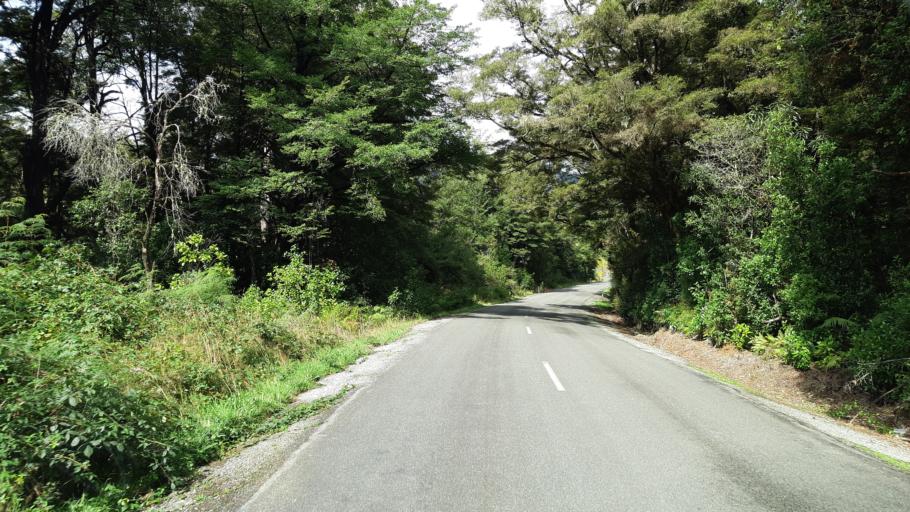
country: NZ
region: West Coast
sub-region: Buller District
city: Westport
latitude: -41.7744
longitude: 172.3735
